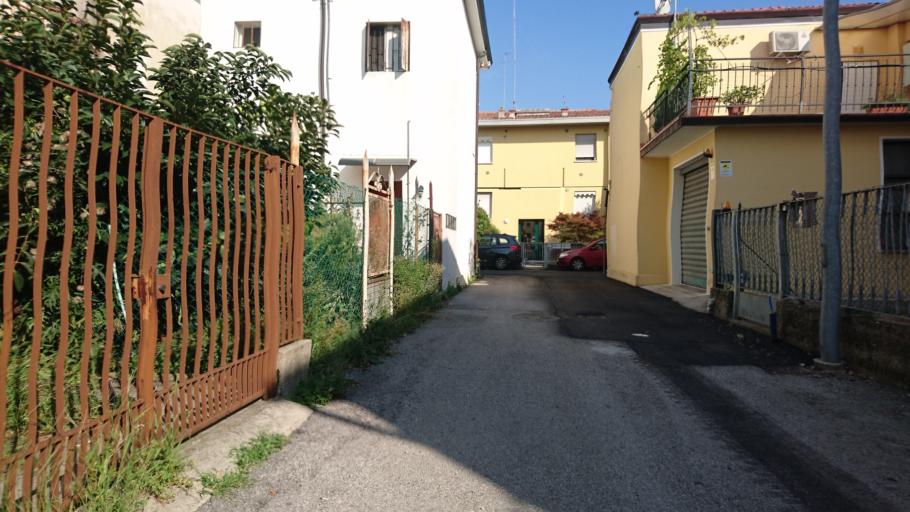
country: IT
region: Veneto
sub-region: Provincia di Padova
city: Padova
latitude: 45.4187
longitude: 11.8865
